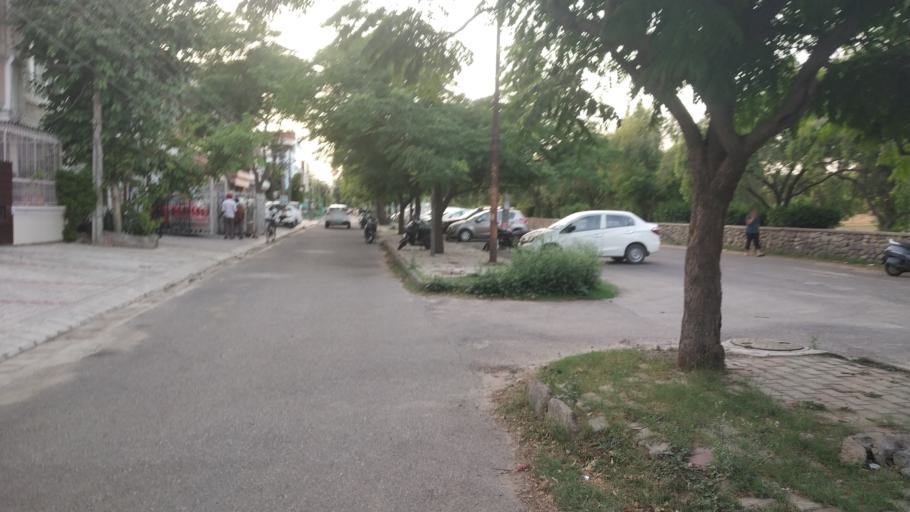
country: IN
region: Punjab
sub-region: Ajitgarh
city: Mohali
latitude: 30.6857
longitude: 76.7307
